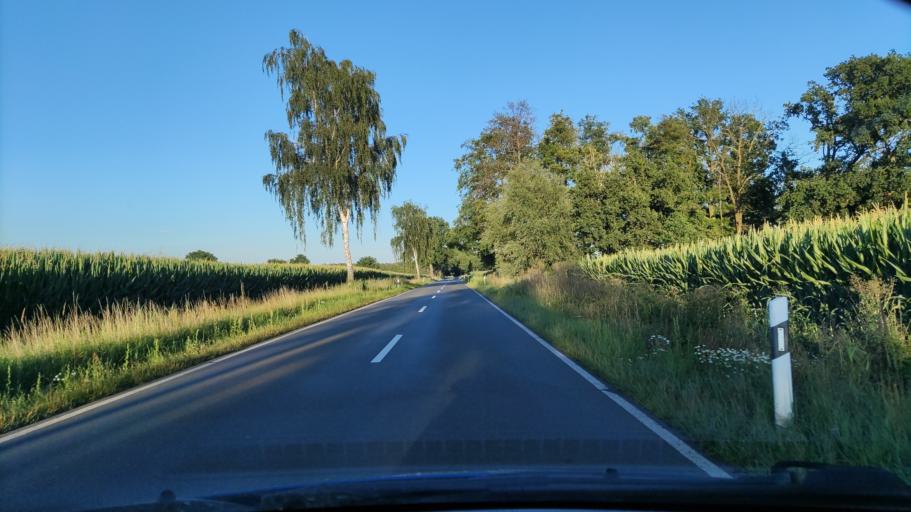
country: DE
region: Lower Saxony
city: Jameln
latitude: 53.0257
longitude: 11.1356
